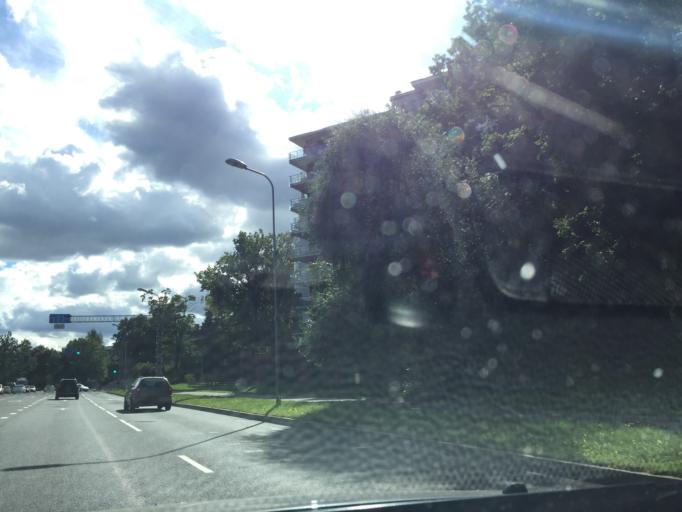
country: LV
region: Riga
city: Bergi
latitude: 56.9871
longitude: 24.2480
